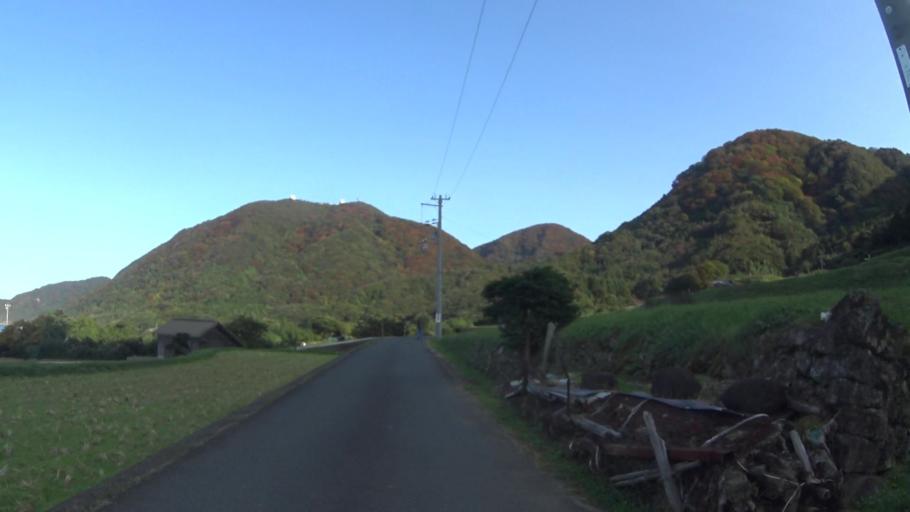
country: JP
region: Kyoto
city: Miyazu
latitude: 35.7619
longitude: 135.2018
